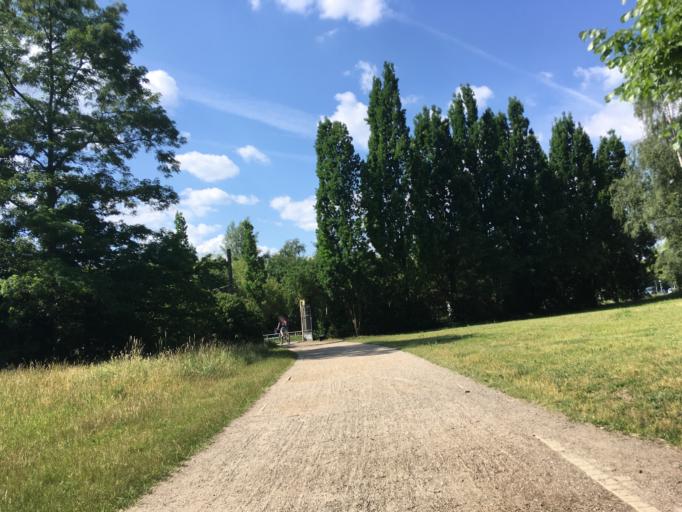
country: DE
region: Berlin
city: Marzahn
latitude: 52.5501
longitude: 13.5855
